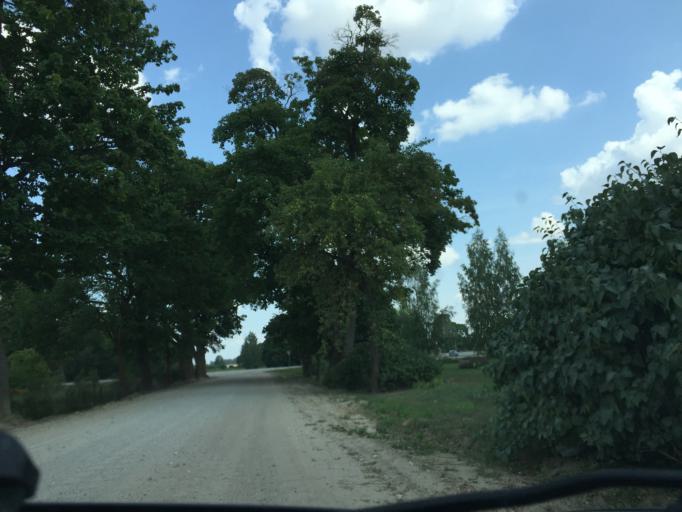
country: LT
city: Zagare
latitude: 56.4001
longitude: 23.2505
